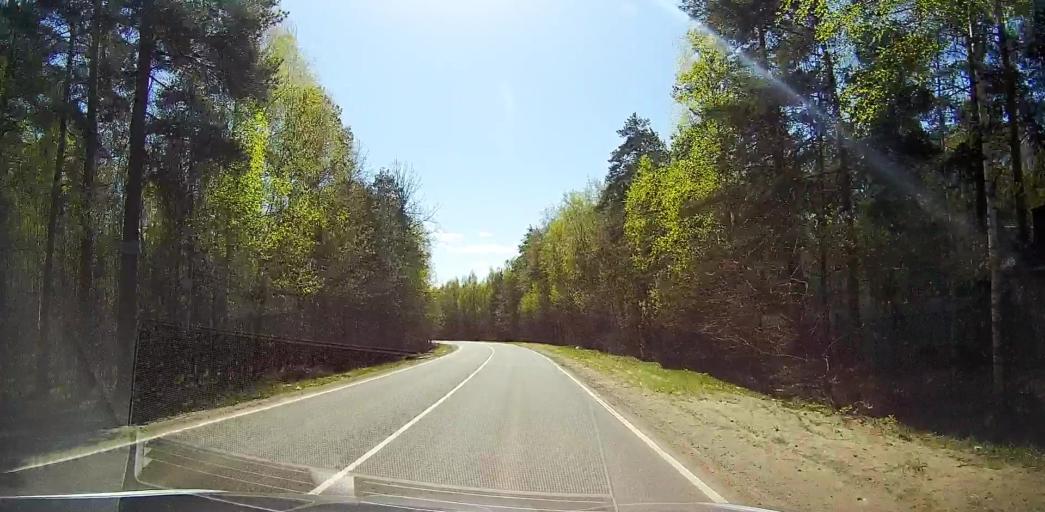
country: RU
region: Moskovskaya
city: Beloozerskiy
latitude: 55.4923
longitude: 38.4275
